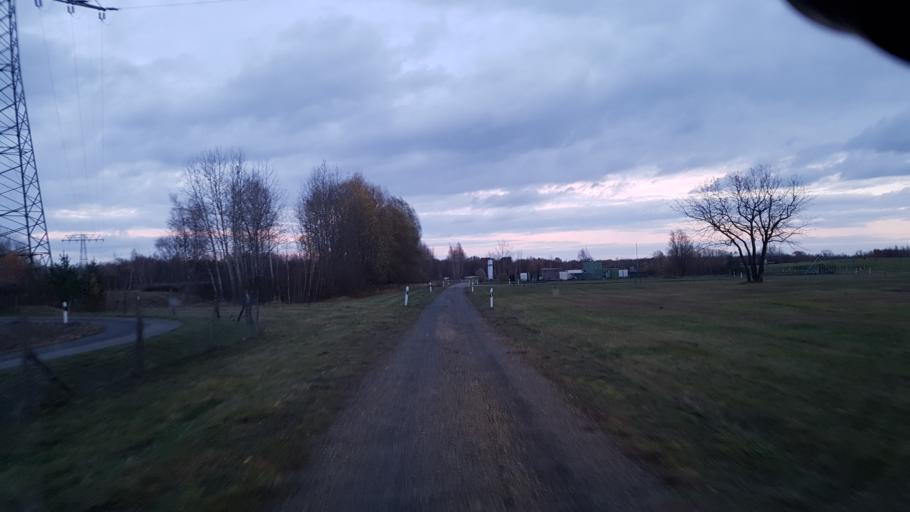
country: DE
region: Brandenburg
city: Lauchhammer
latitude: 51.4886
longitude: 13.7187
